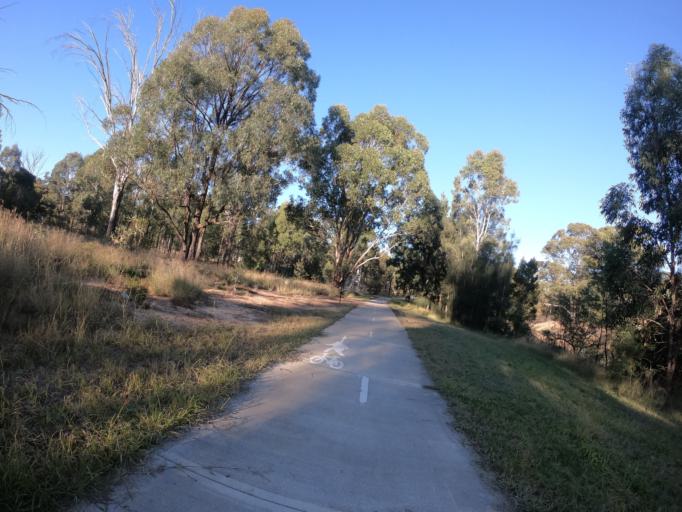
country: AU
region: New South Wales
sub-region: Hawkesbury
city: South Windsor
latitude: -33.6350
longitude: 150.8112
